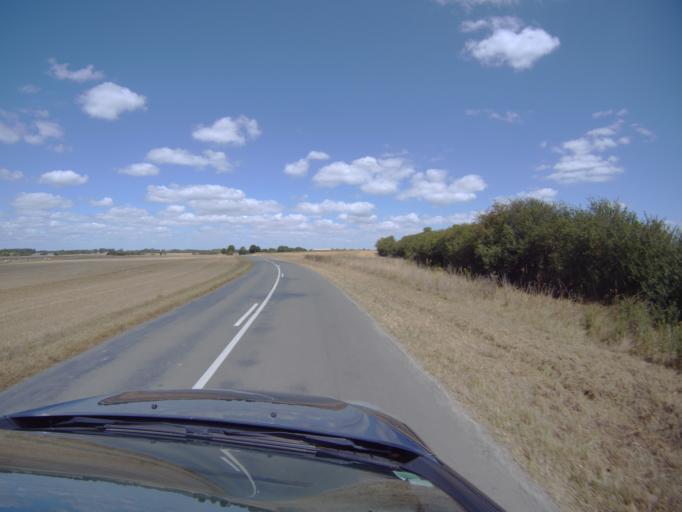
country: FR
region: Poitou-Charentes
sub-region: Departement des Deux-Sevres
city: Saint-Hilaire-la-Palud
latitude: 46.2602
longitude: -0.7287
